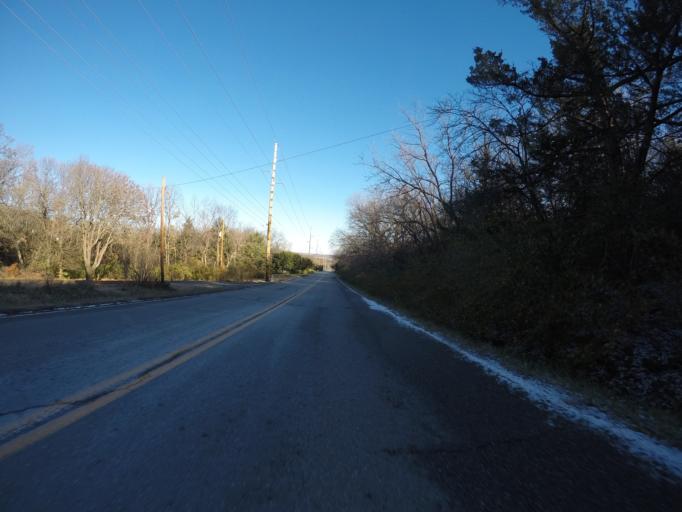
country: US
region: Kansas
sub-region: Riley County
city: Manhattan
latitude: 39.2184
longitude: -96.6156
